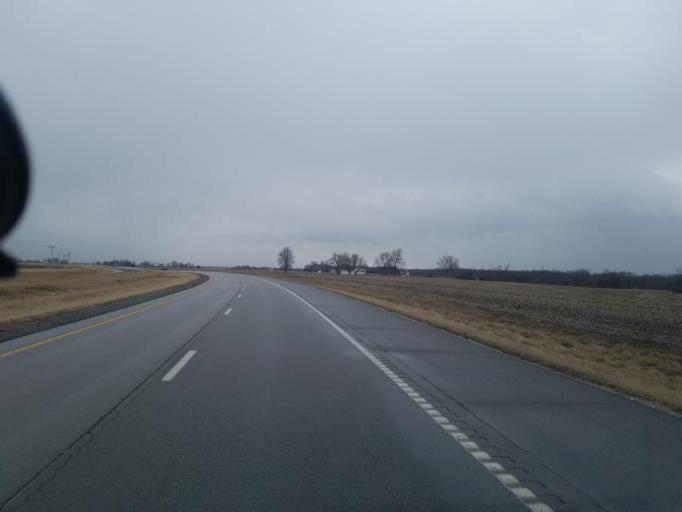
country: US
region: Missouri
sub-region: Macon County
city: Macon
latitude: 39.8446
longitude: -92.4813
